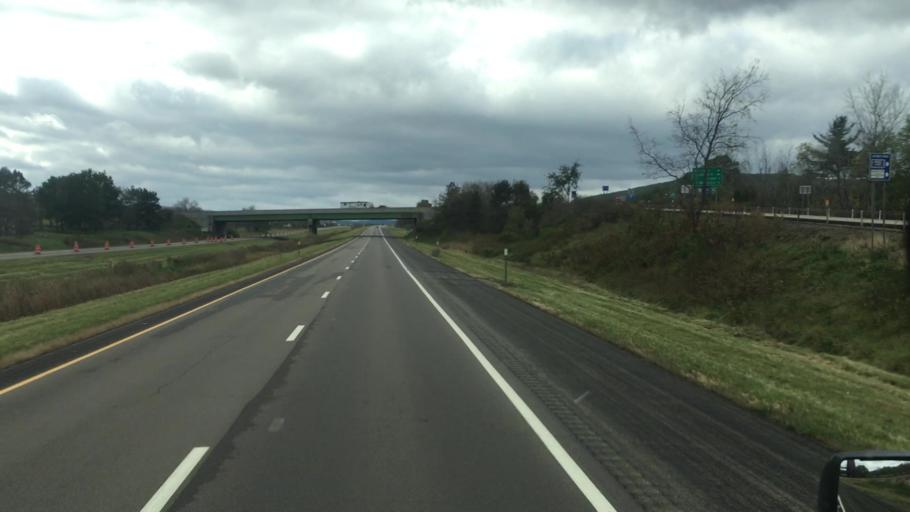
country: US
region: New York
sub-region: Allegany County
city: Belmont
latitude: 42.2621
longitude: -78.0613
